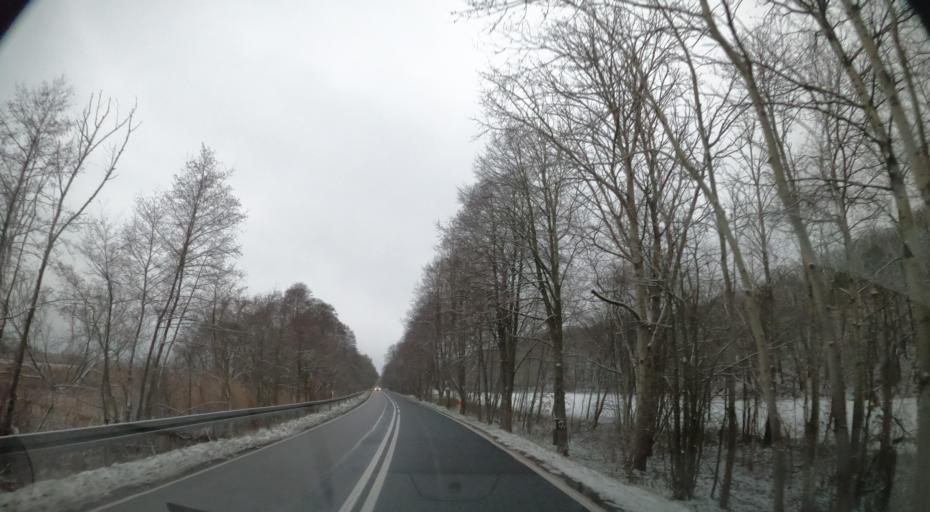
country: PL
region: Masovian Voivodeship
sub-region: Powiat plocki
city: Nowy Duninow
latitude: 52.5769
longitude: 19.5480
